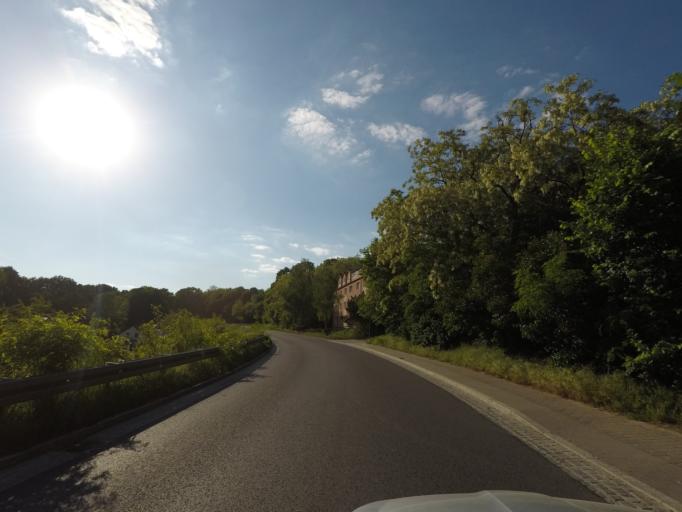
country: DE
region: Brandenburg
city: Falkenberg
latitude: 52.8048
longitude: 13.9478
